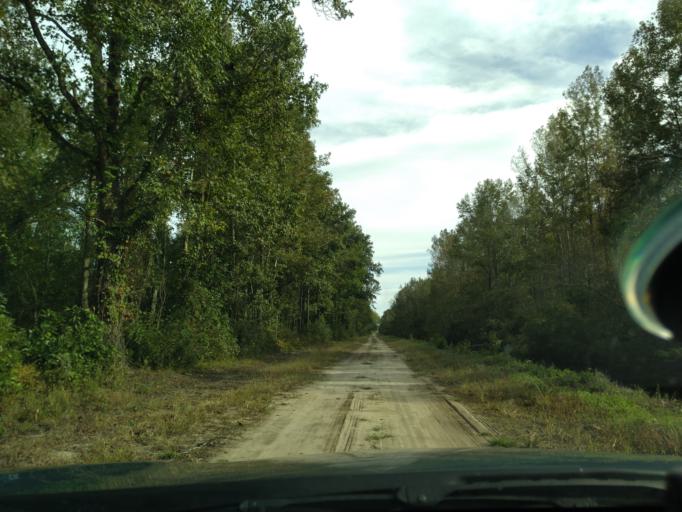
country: US
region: North Carolina
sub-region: Beaufort County
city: Belhaven
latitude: 35.6986
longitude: -76.5623
